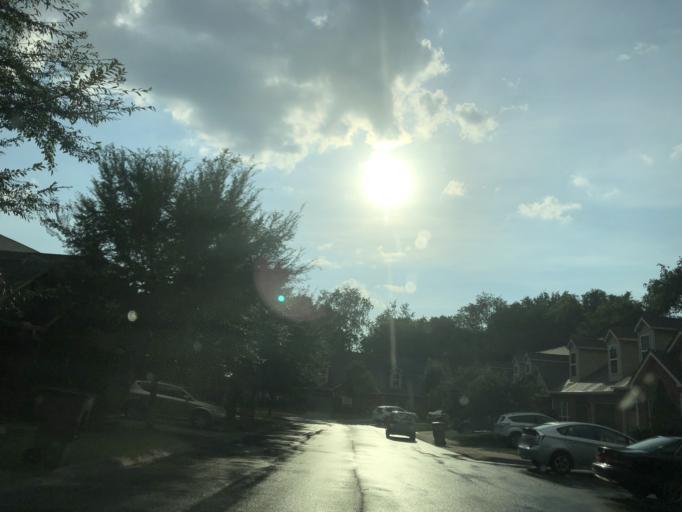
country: US
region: Tennessee
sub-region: Davidson County
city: Lakewood
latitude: 36.1544
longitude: -86.6677
